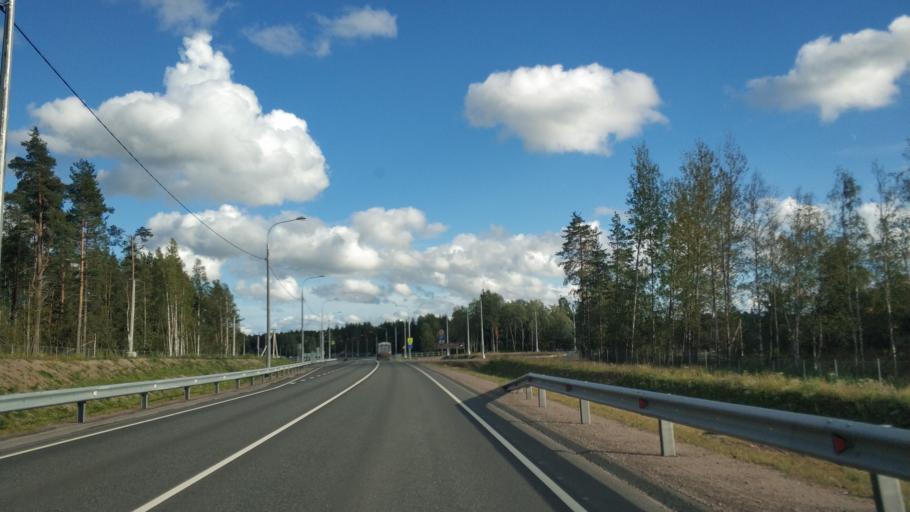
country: RU
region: Leningrad
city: Kuznechnoye
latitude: 61.1003
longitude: 29.9717
